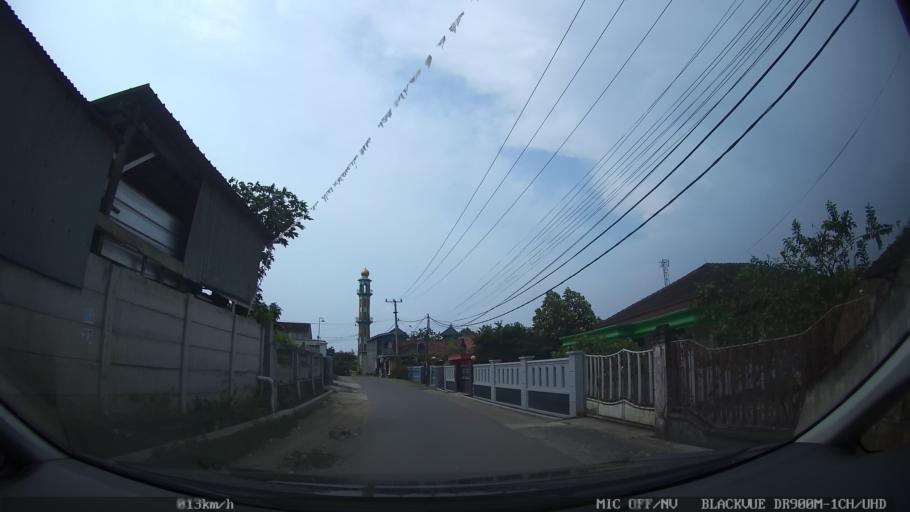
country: ID
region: Lampung
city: Bandarlampung
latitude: -5.4237
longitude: 105.2832
